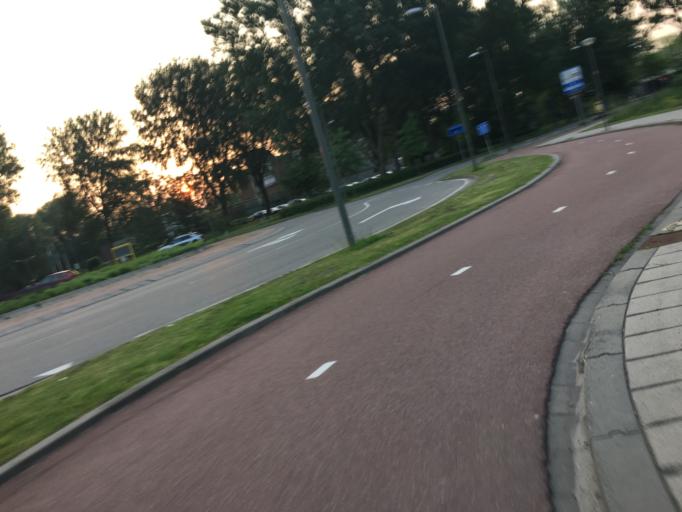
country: NL
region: South Holland
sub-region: Gemeente Schiedam
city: Schiedam
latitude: 51.9236
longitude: 4.3771
